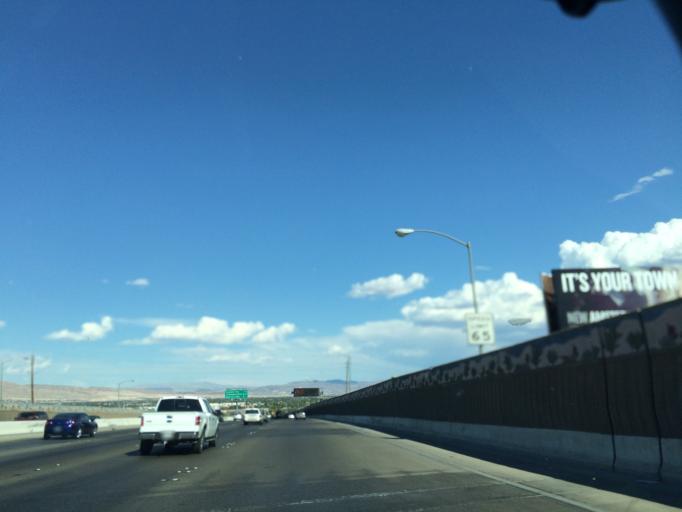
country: US
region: Nevada
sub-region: Clark County
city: Las Vegas
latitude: 36.1700
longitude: -115.1299
